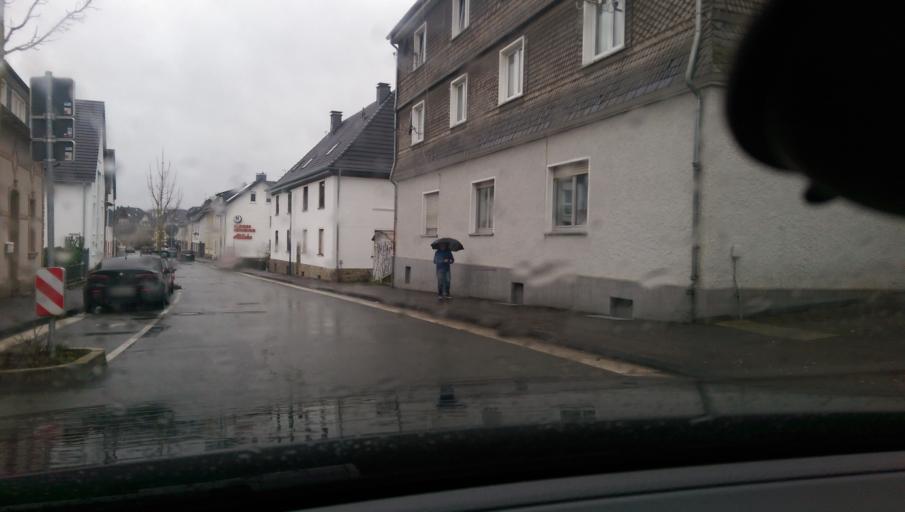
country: DE
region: North Rhine-Westphalia
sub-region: Regierungsbezirk Arnsberg
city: Attendorn
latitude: 51.1276
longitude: 7.9098
